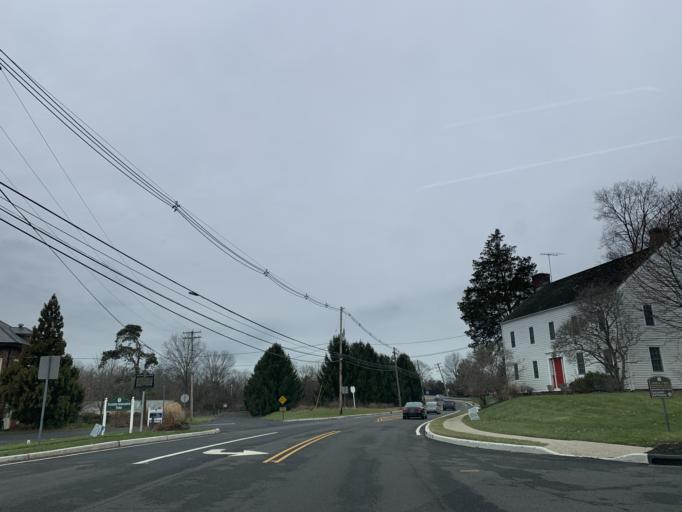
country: US
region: New Jersey
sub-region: Somerset County
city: Bedminster
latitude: 40.6463
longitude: -74.6432
